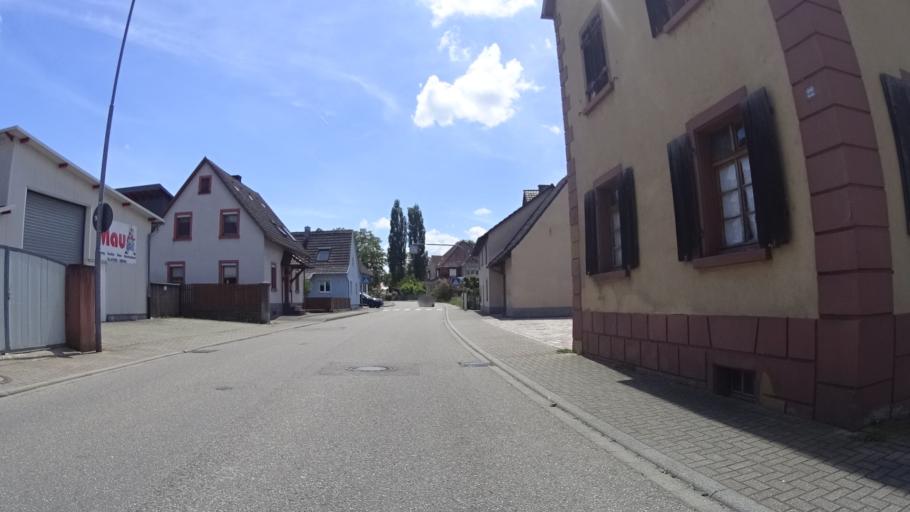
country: DE
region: Baden-Wuerttemberg
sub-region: Freiburg Region
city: Rust
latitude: 48.2900
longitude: 7.7411
